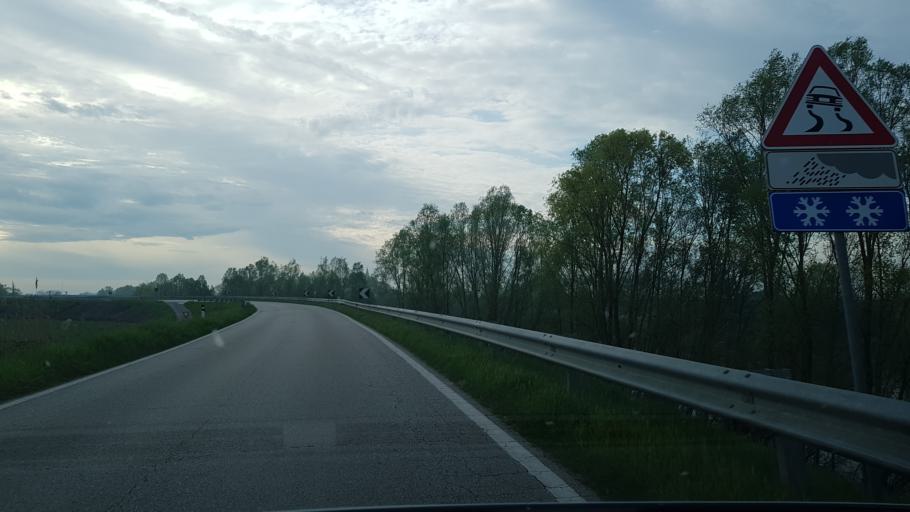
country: IT
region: Veneto
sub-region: Provincia di Rovigo
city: Lusia
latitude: 45.1072
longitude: 11.6545
